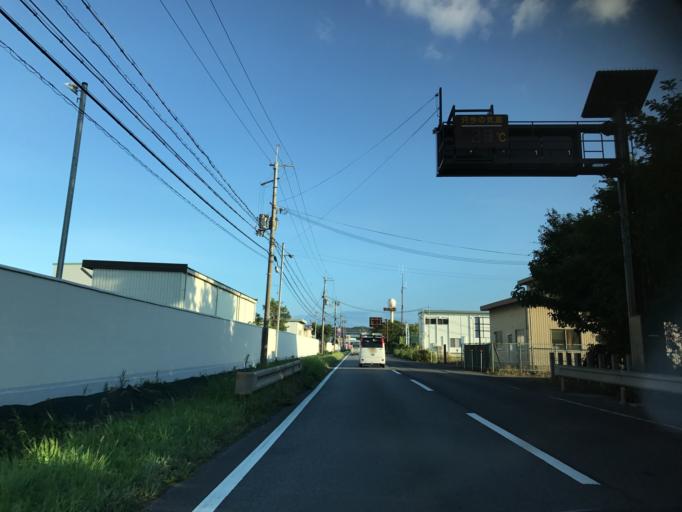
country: JP
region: Shiga Prefecture
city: Youkaichi
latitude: 35.0869
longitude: 136.2502
